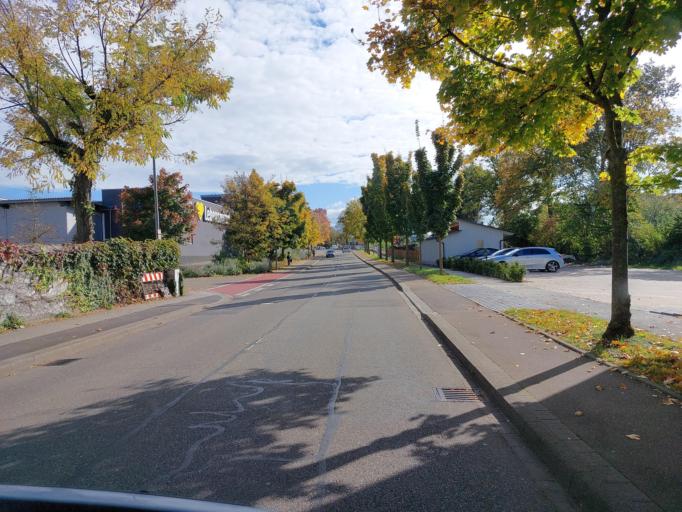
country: DE
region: Baden-Wuerttemberg
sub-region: Freiburg Region
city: Teningen
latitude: 48.1304
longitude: 7.8100
